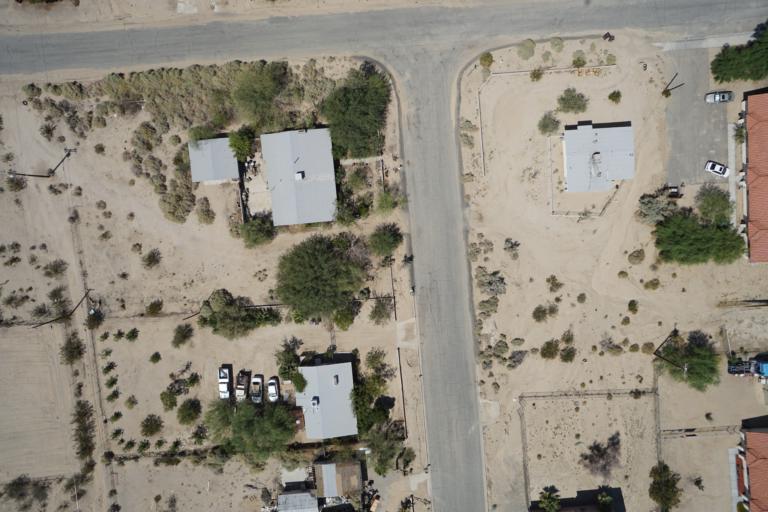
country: US
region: California
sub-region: San Bernardino County
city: Twentynine Palms
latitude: 34.1316
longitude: -116.0532
